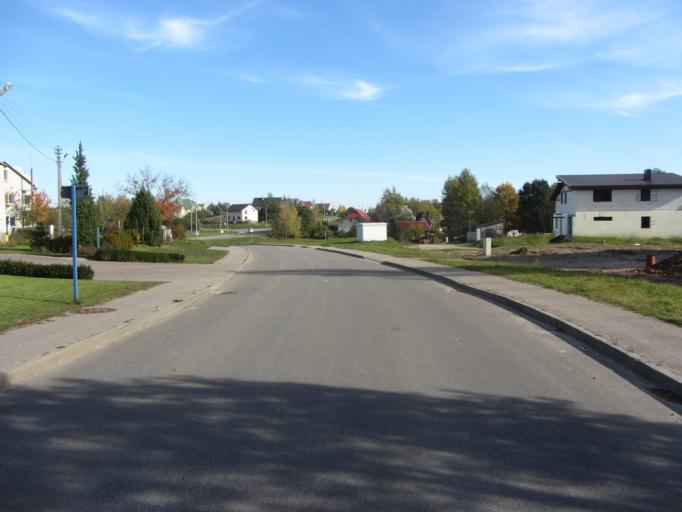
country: LT
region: Vilnius County
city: Elektrenai
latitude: 54.7796
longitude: 24.7015
